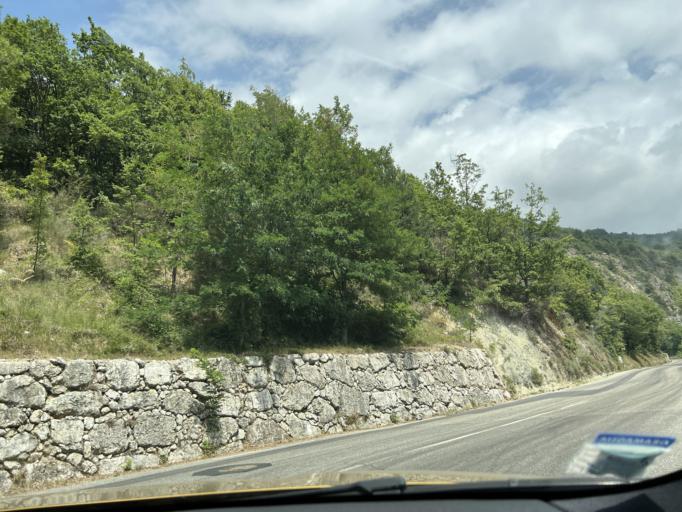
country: FR
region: Provence-Alpes-Cote d'Azur
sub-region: Departement des Alpes-Maritimes
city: Tourrettes-sur-Loup
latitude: 43.7957
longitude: 6.9523
